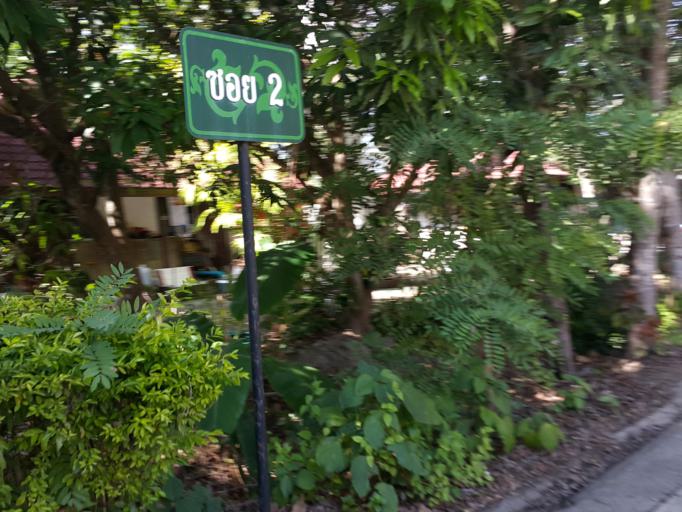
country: TH
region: Chiang Mai
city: San Sai
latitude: 18.8640
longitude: 99.1120
